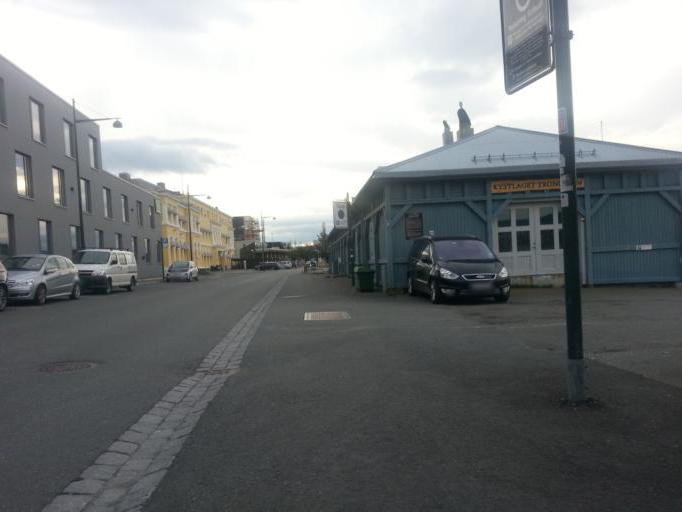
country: NO
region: Sor-Trondelag
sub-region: Trondheim
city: Trondheim
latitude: 63.4358
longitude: 10.3958
